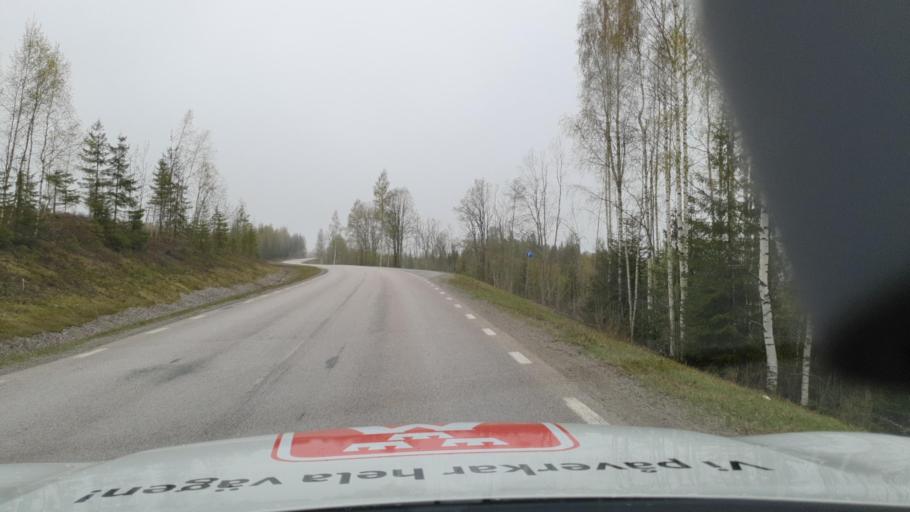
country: SE
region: Vaesterbotten
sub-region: Vannas Kommun
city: Vaennaes
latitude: 63.7897
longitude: 19.8237
